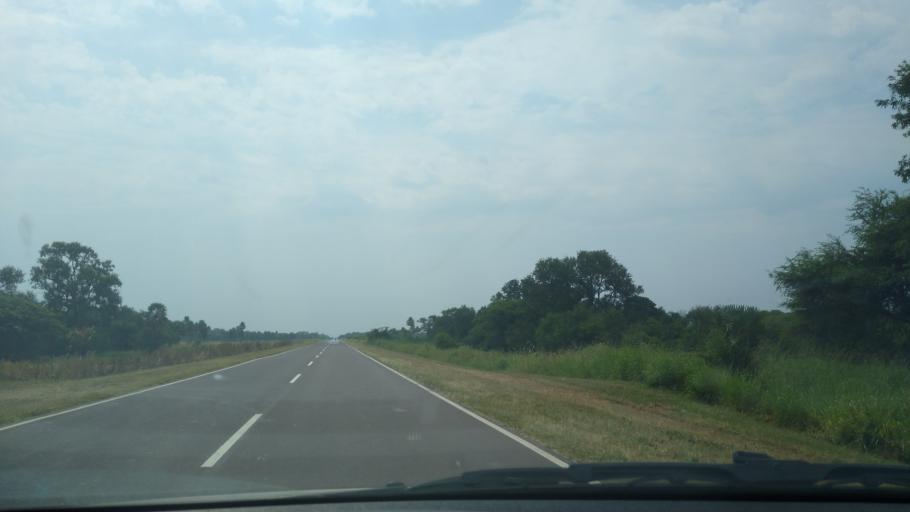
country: AR
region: Chaco
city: La Eduvigis
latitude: -27.0386
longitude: -58.9641
